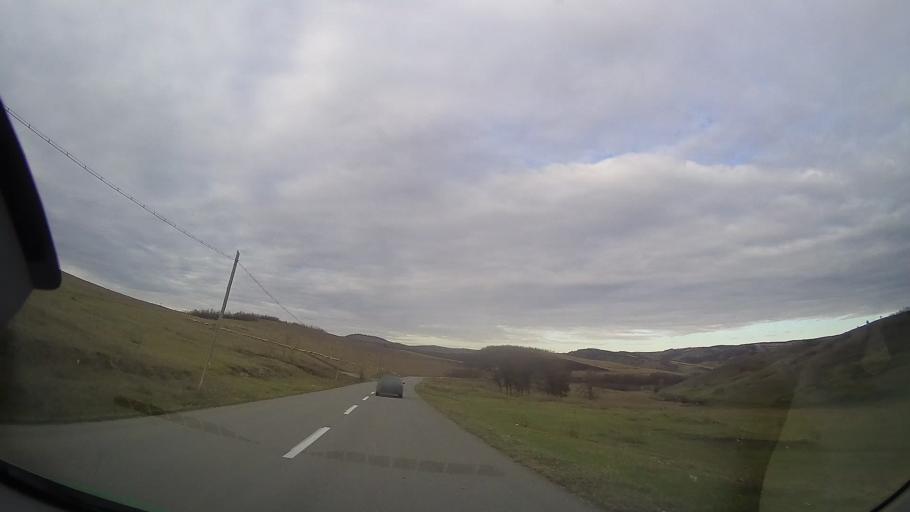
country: RO
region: Bistrita-Nasaud
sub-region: Comuna Milas
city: Milas
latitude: 46.8265
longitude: 24.4520
